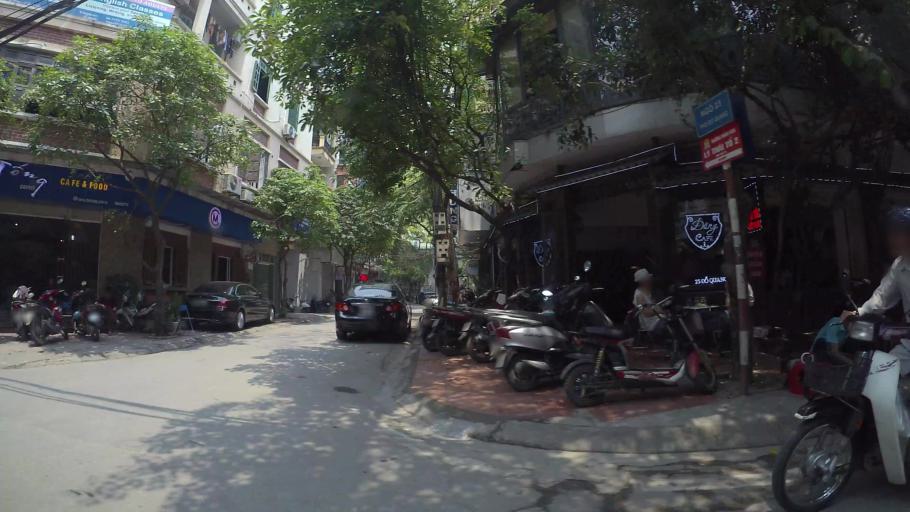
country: VN
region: Ha Noi
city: Thanh Xuan
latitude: 21.0110
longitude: 105.8021
